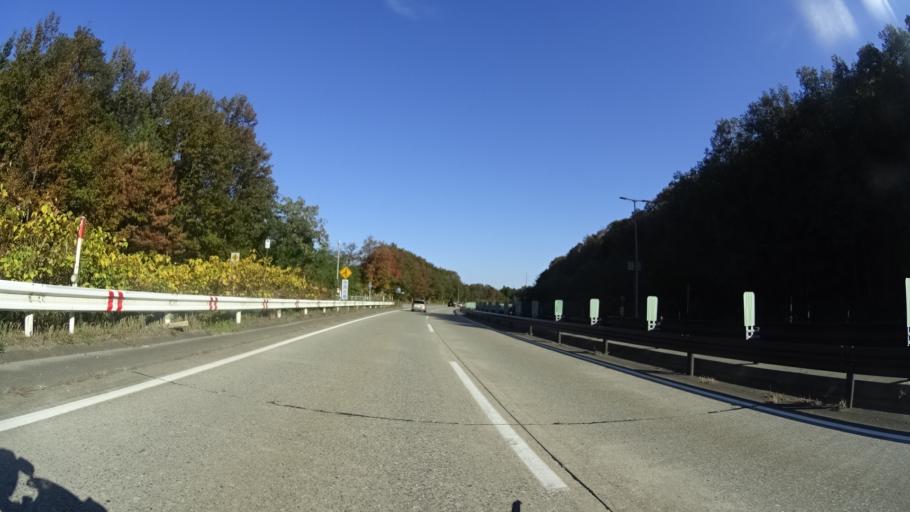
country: JP
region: Ishikawa
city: Komatsu
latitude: 36.3568
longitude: 136.4522
